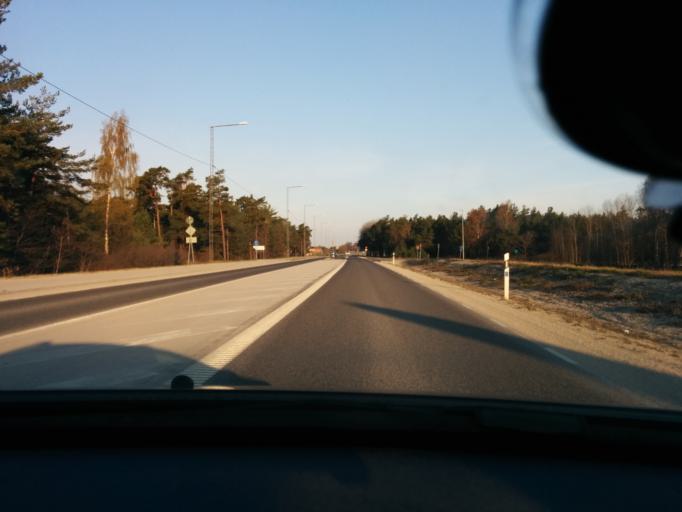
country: SE
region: Gotland
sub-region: Gotland
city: Visby
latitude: 57.6314
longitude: 18.3359
